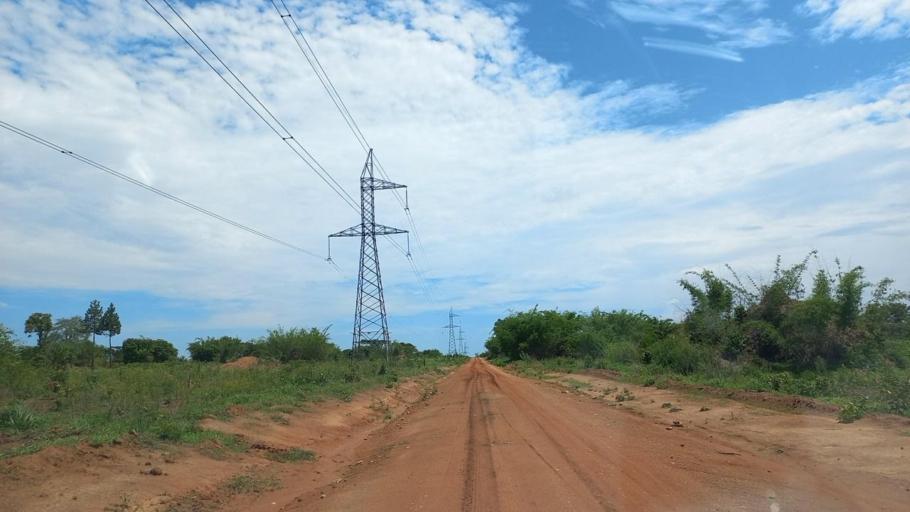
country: ZM
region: Copperbelt
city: Kitwe
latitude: -12.8224
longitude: 28.3517
